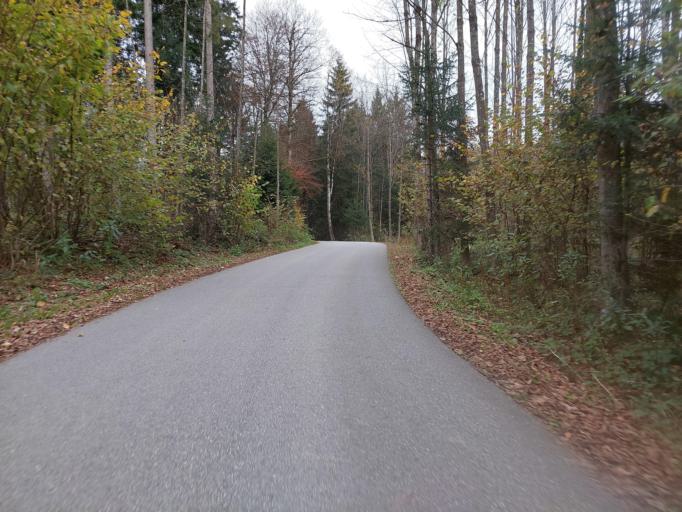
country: AT
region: Tyrol
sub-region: Politischer Bezirk Kufstein
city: Angath
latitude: 47.5005
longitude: 12.0421
